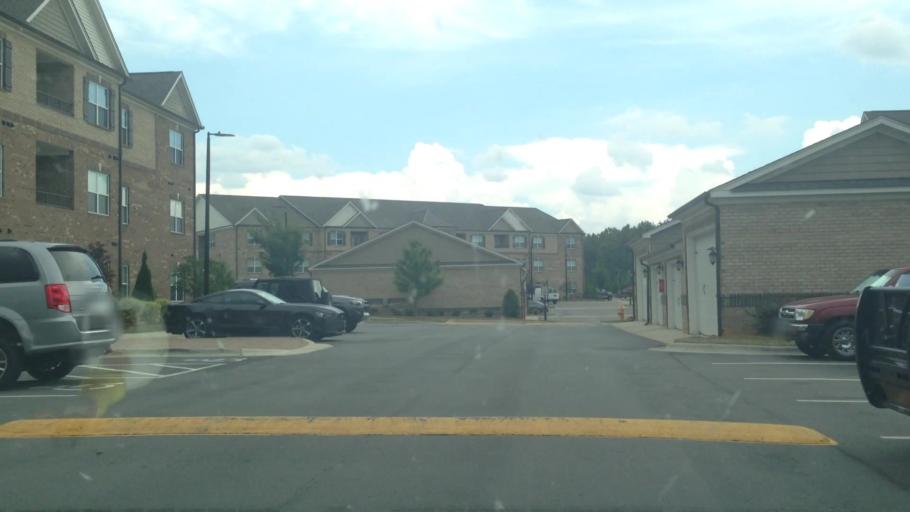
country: US
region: North Carolina
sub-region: Forsyth County
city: Walkertown
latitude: 36.1657
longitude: -80.1343
